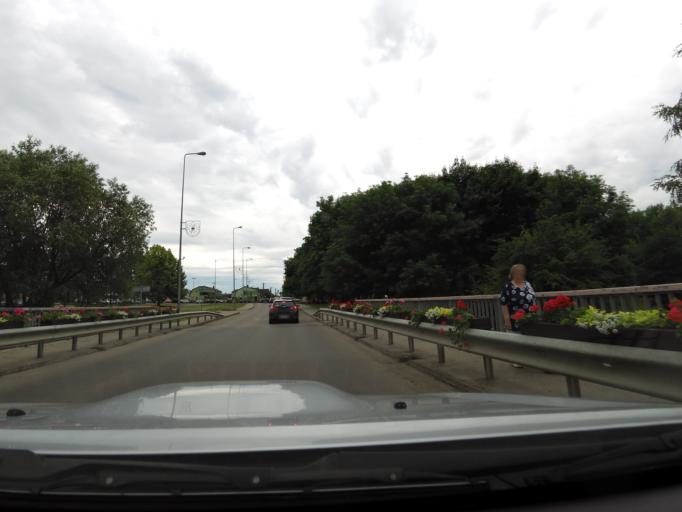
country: LT
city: Vilkaviskis
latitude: 54.6499
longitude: 23.0322
